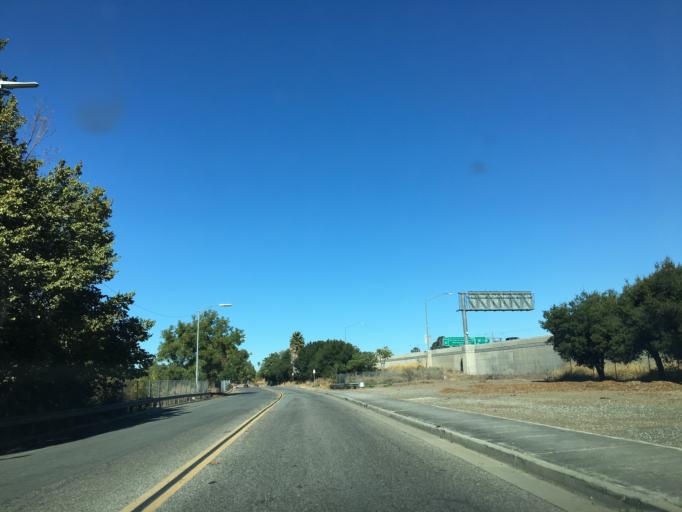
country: US
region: California
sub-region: Santa Clara County
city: San Jose
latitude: 37.3129
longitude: -121.8870
